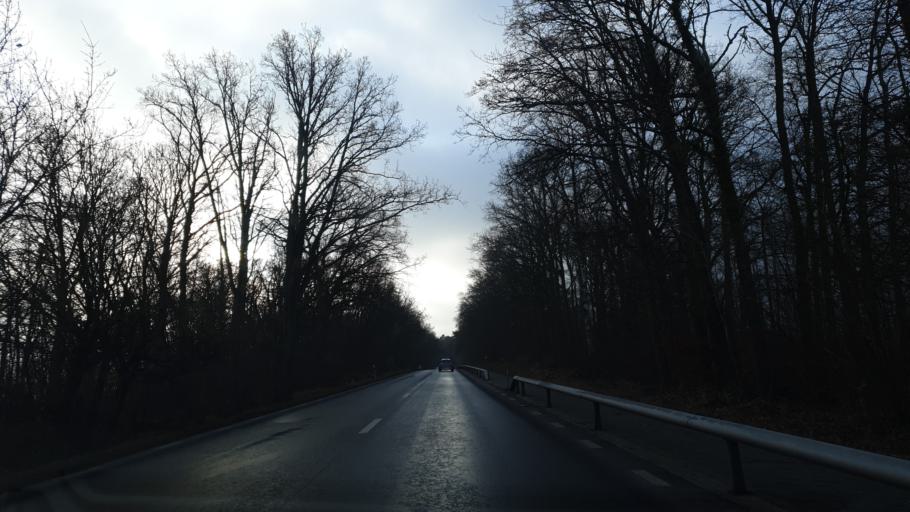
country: SE
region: Blekinge
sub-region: Karlshamns Kommun
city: Morrum
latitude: 56.1298
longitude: 14.6731
